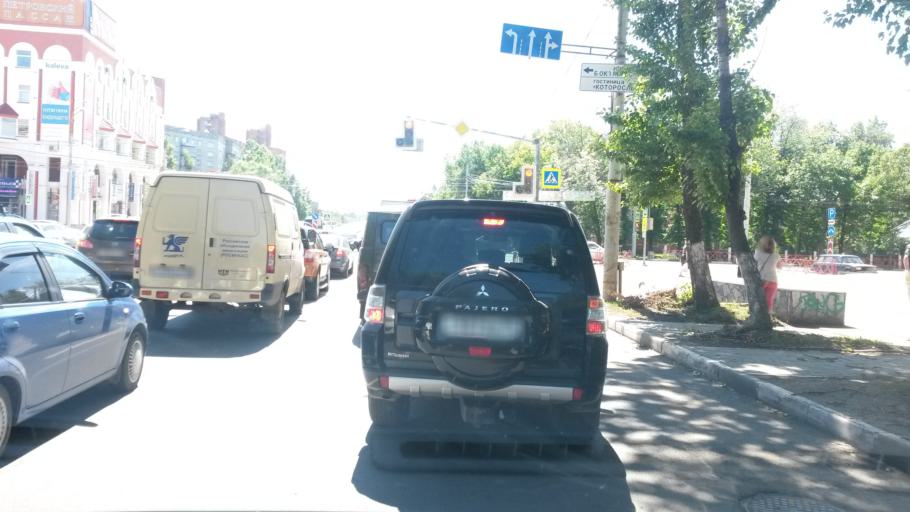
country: RU
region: Jaroslavl
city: Yaroslavl
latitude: 57.6214
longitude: 39.8580
